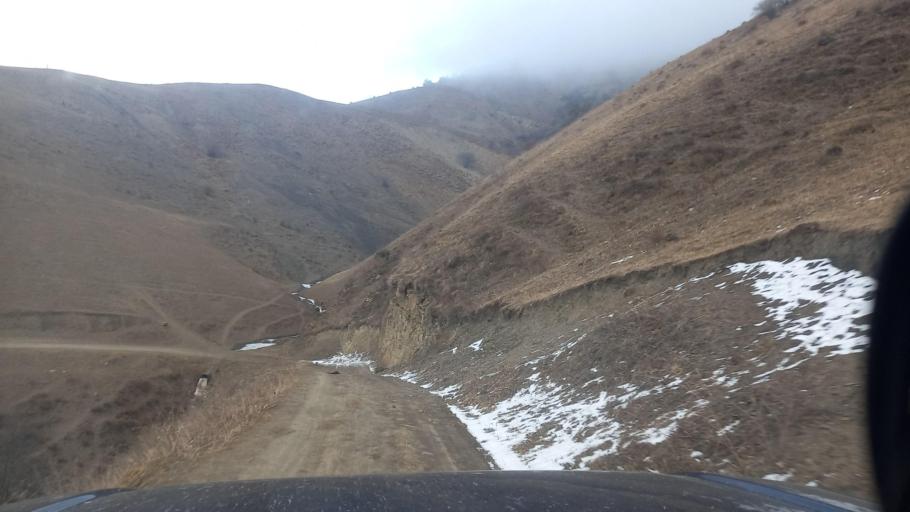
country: RU
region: Ingushetiya
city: Dzhayrakh
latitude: 42.8049
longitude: 44.7608
